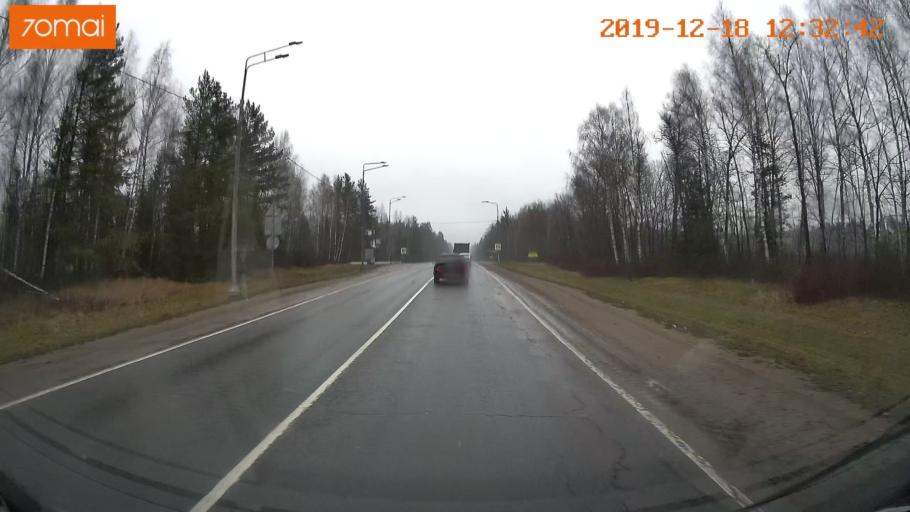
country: RU
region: Moskovskaya
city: Rumyantsevo
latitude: 56.1075
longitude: 36.5536
